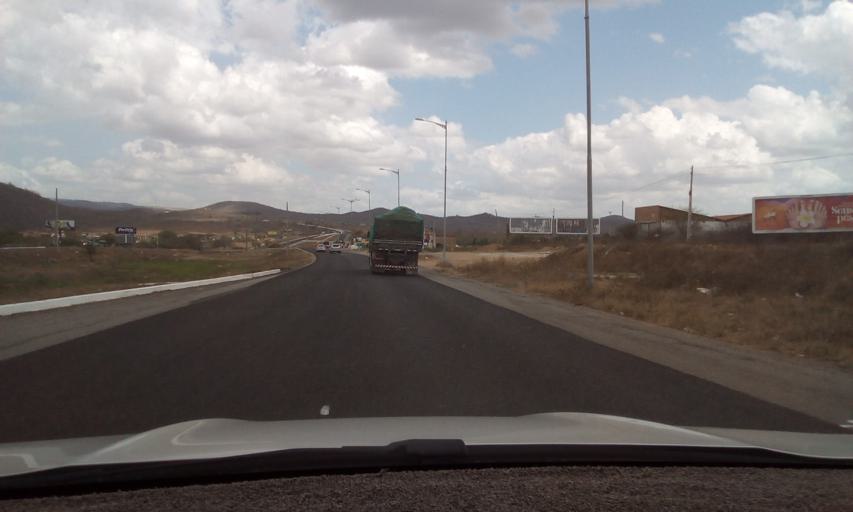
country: BR
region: Pernambuco
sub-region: Toritama
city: Toritama
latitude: -8.1059
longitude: -36.0232
